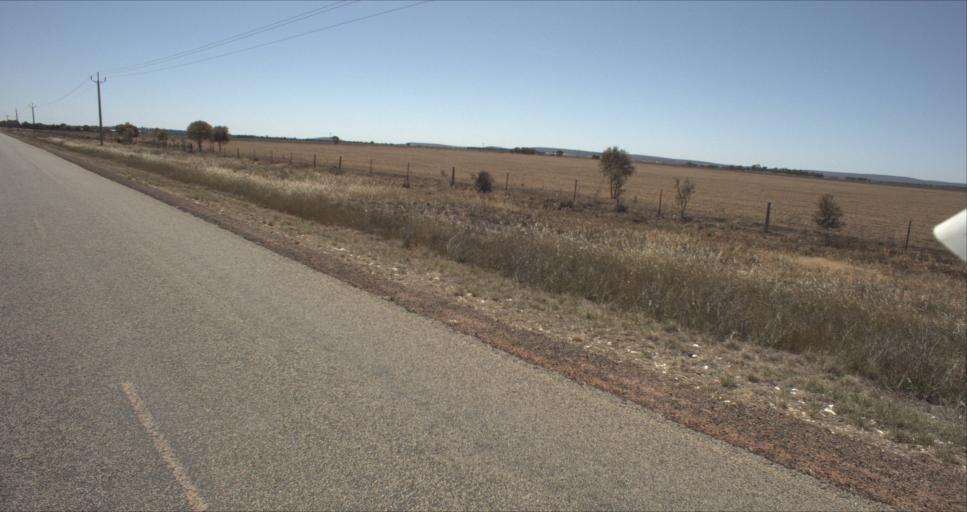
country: AU
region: New South Wales
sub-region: Leeton
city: Leeton
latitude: -34.4611
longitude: 146.2941
